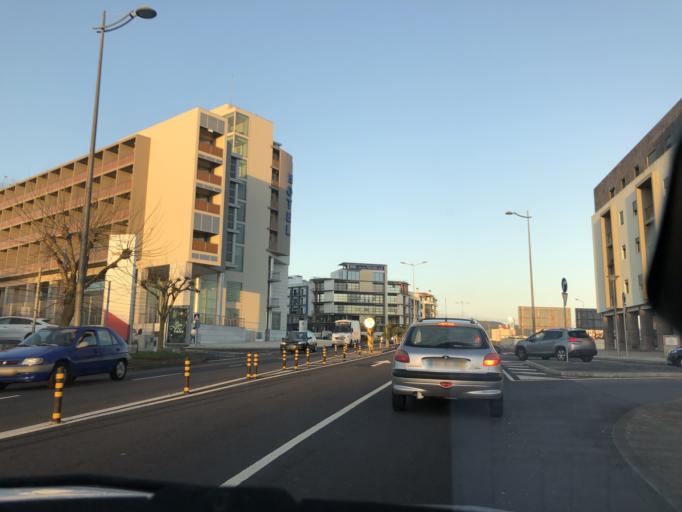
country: PT
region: Azores
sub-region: Ponta Delgada
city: Rosto de Cao
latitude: 37.7501
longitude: -25.6592
